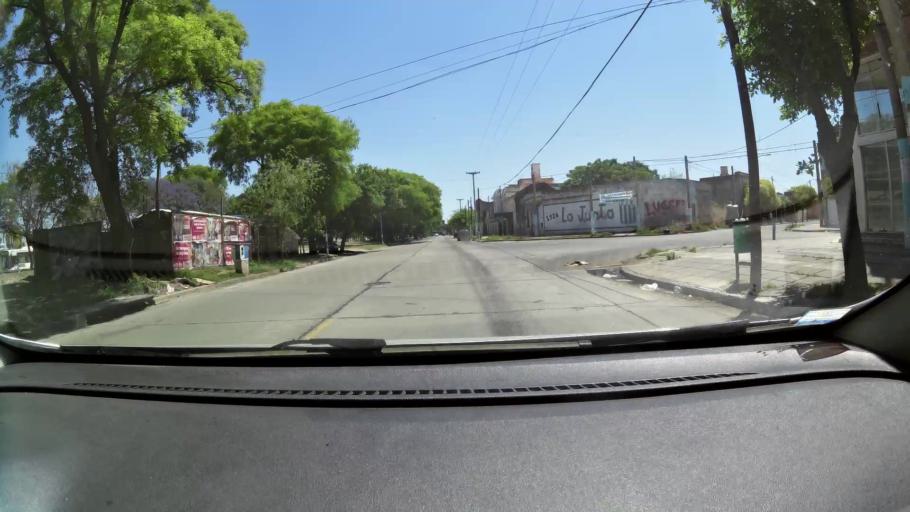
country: AR
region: Cordoba
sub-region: Departamento de Capital
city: Cordoba
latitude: -31.3945
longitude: -64.1559
